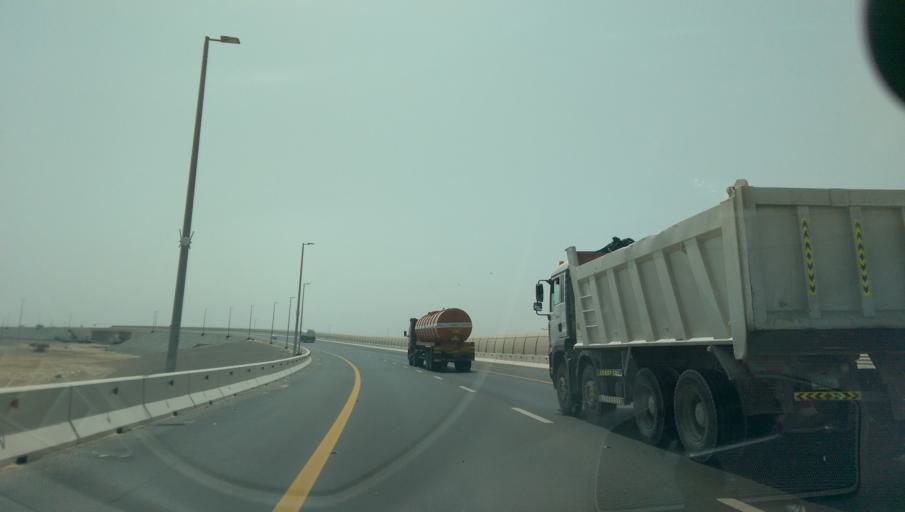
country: AE
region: Abu Dhabi
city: Abu Dhabi
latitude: 24.2839
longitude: 54.5521
